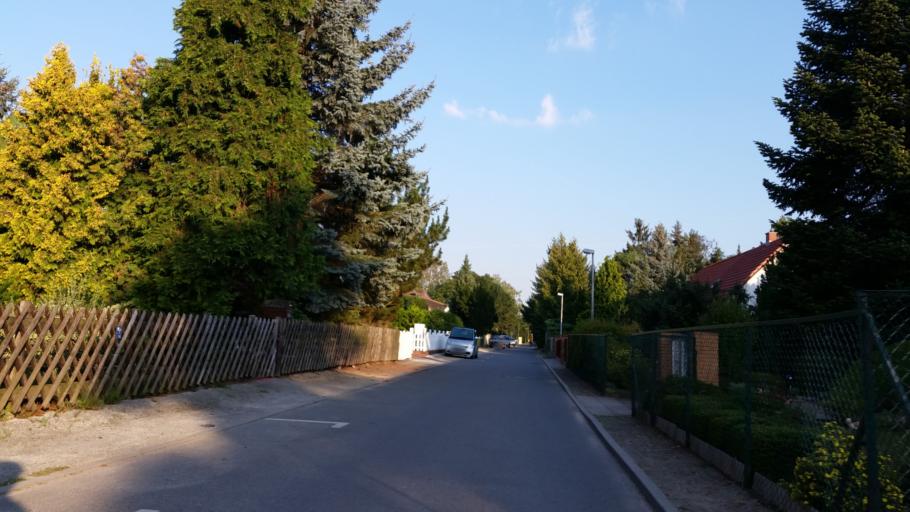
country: DE
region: Berlin
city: Marienfelde
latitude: 52.4011
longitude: 13.3555
